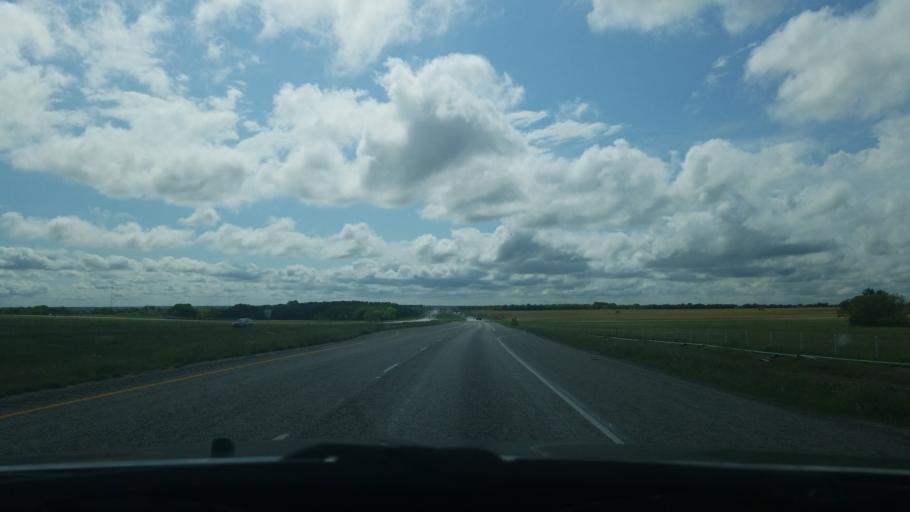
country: US
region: Texas
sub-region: Denton County
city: Ponder
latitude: 33.2395
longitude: -97.3380
